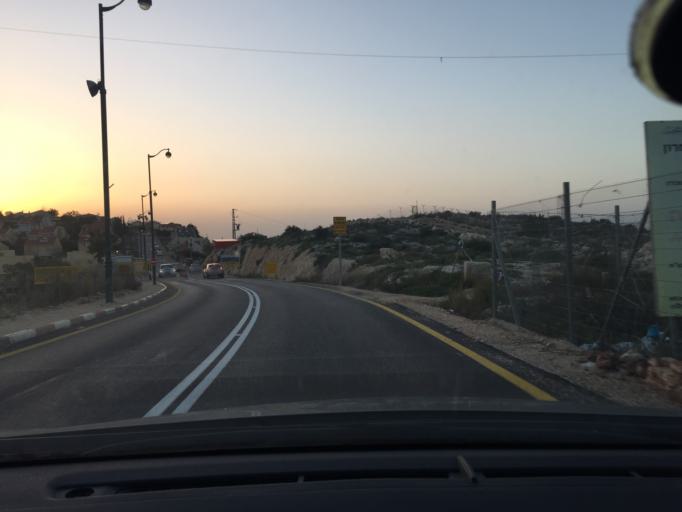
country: PS
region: West Bank
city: Rafat
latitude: 32.0652
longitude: 35.0588
